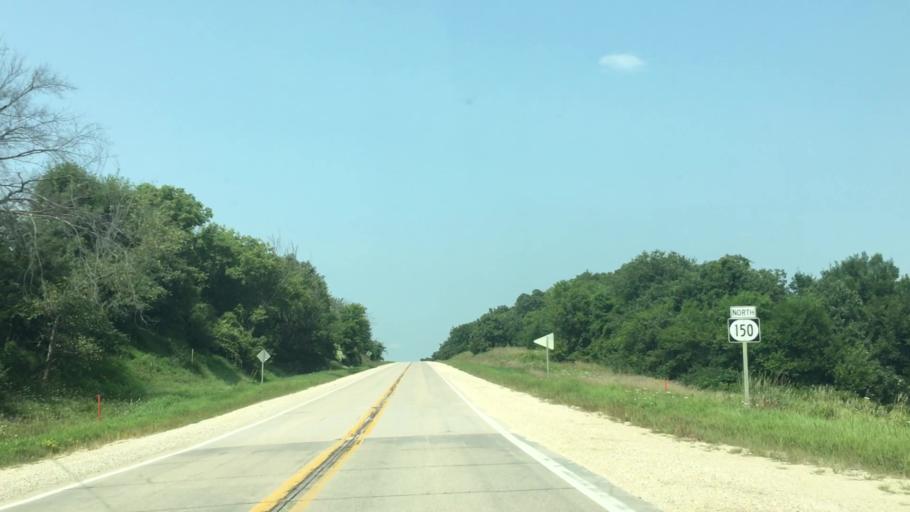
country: US
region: Iowa
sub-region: Fayette County
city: West Union
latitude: 43.1214
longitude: -91.8698
